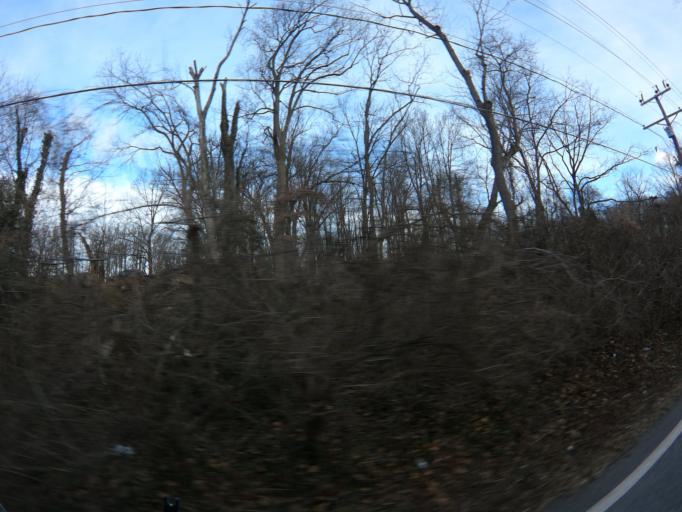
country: US
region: Maryland
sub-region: Montgomery County
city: Ashton-Sandy Spring
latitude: 39.1509
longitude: -77.0083
